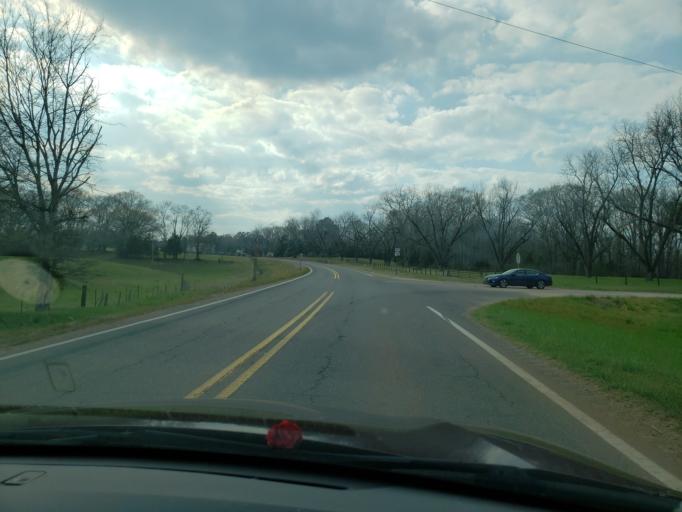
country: US
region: Alabama
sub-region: Hale County
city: Greensboro
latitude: 32.7224
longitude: -87.6260
